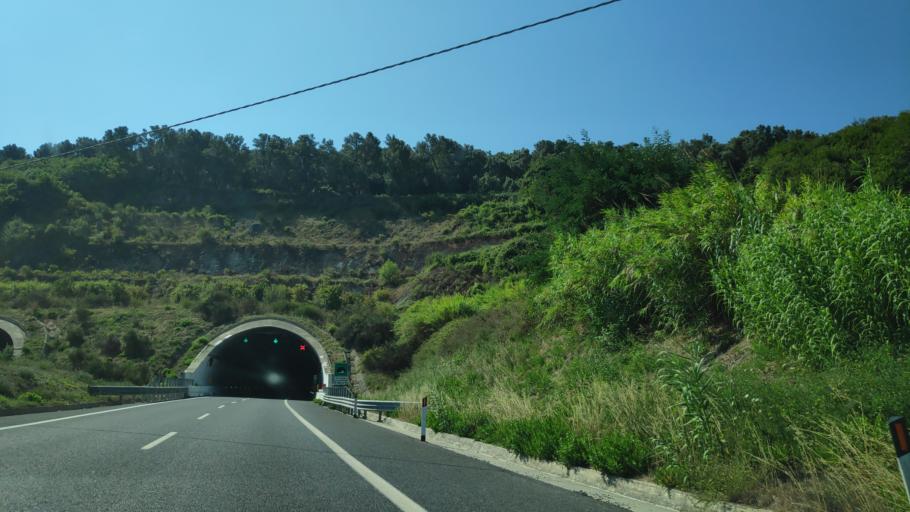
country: IT
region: Calabria
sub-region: Provincia di Reggio Calabria
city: Seminara
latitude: 38.3542
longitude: 15.8679
